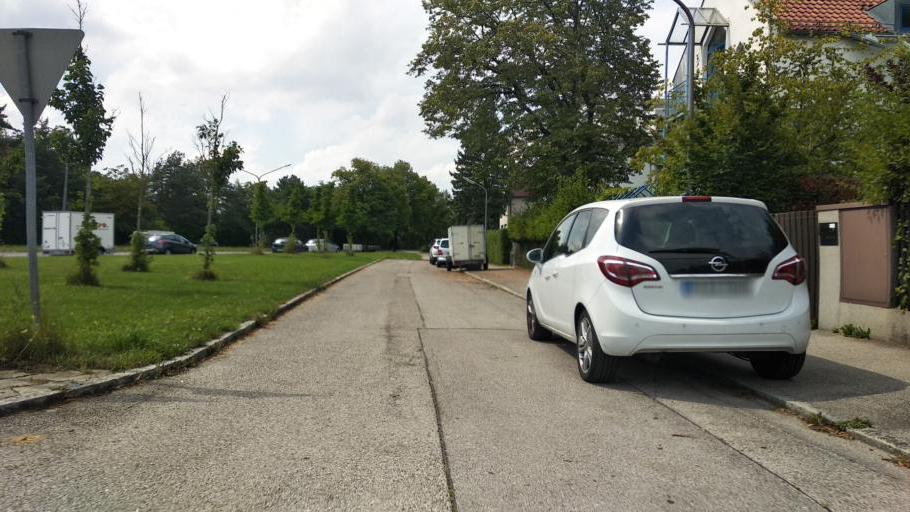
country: DE
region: Bavaria
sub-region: Upper Bavaria
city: Neubiberg
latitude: 48.1153
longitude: 11.6442
